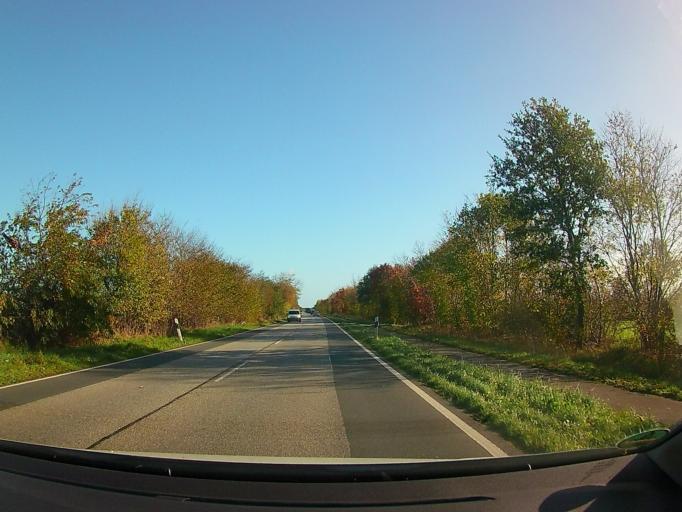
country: DE
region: Schleswig-Holstein
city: Schuby
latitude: 54.5170
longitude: 9.4405
